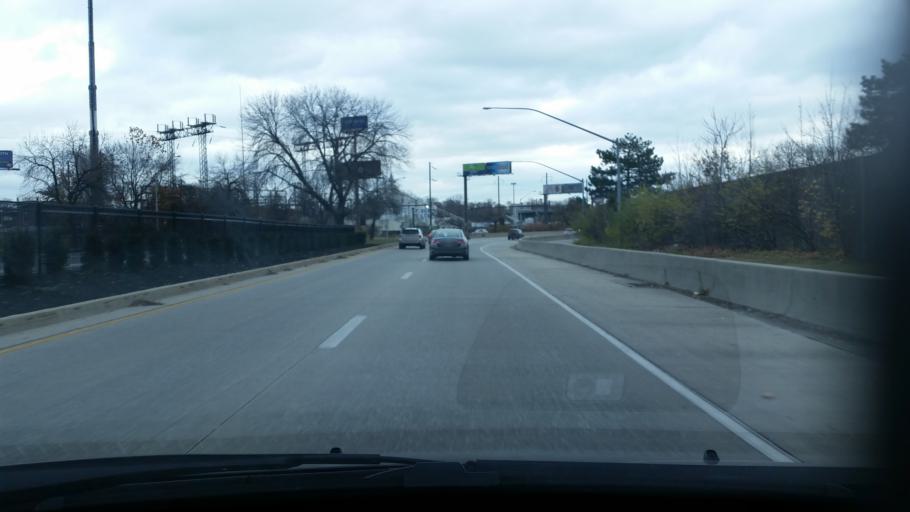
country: US
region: Pennsylvania
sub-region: Dauphin County
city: Harrisburg
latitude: 40.2551
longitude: -76.8762
